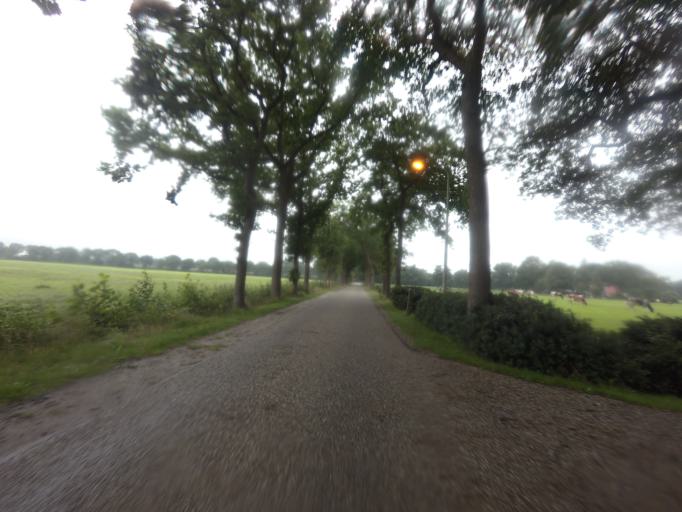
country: NL
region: Friesland
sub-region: Gemeente Heerenveen
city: Nieuwehorne
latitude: 52.9537
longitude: 6.0770
